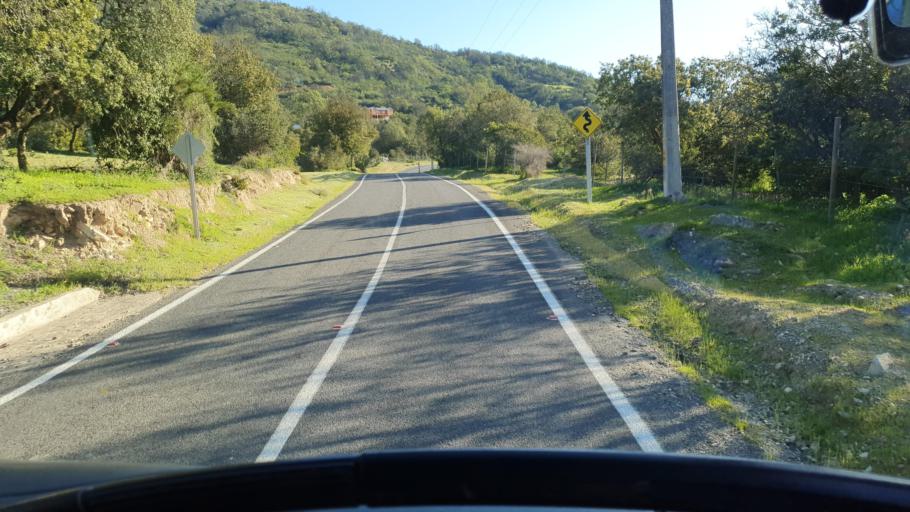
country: CL
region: Valparaiso
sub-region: Provincia de Marga Marga
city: Limache
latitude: -33.2022
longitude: -71.2426
